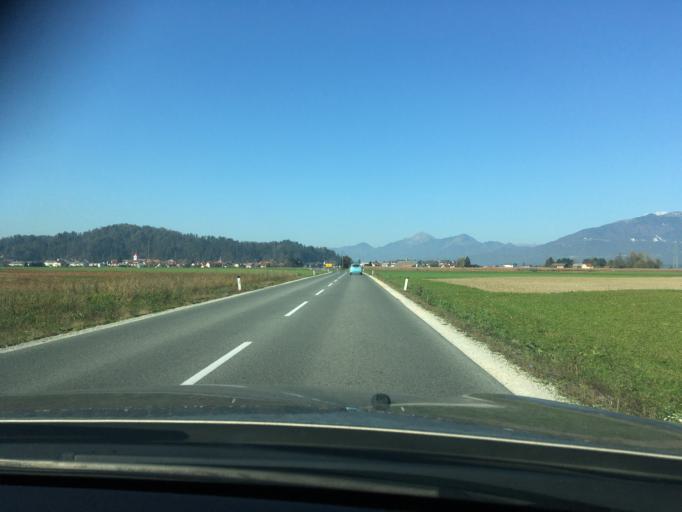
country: SI
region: Menges
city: Menges
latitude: 46.1569
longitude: 14.5847
